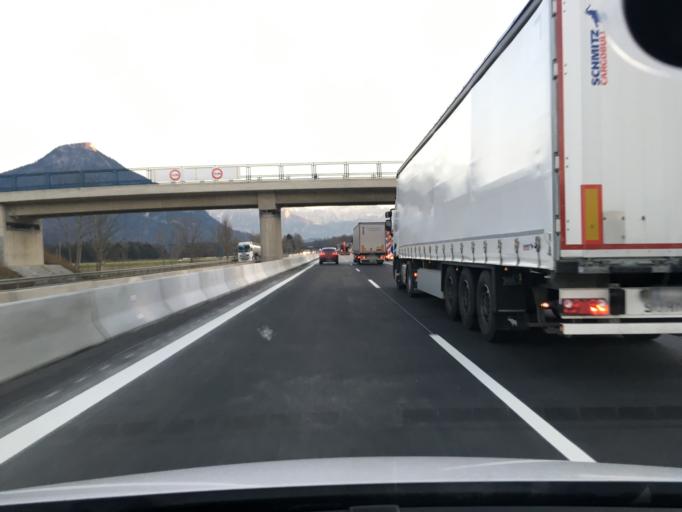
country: DE
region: Bavaria
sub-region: Upper Bavaria
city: Flintsbach
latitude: 47.7297
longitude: 12.1341
